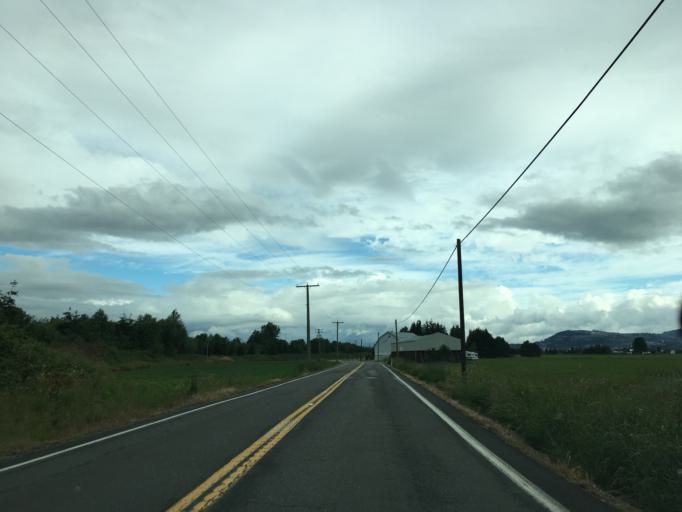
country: US
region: Washington
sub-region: Whatcom County
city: Sumas
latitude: 48.9753
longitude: -122.2339
